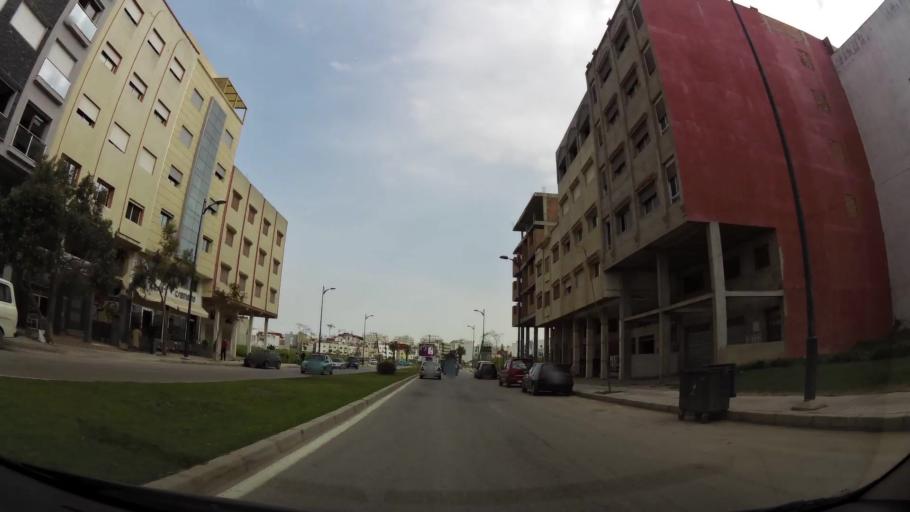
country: MA
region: Tanger-Tetouan
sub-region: Tanger-Assilah
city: Tangier
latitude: 35.7515
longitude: -5.8470
